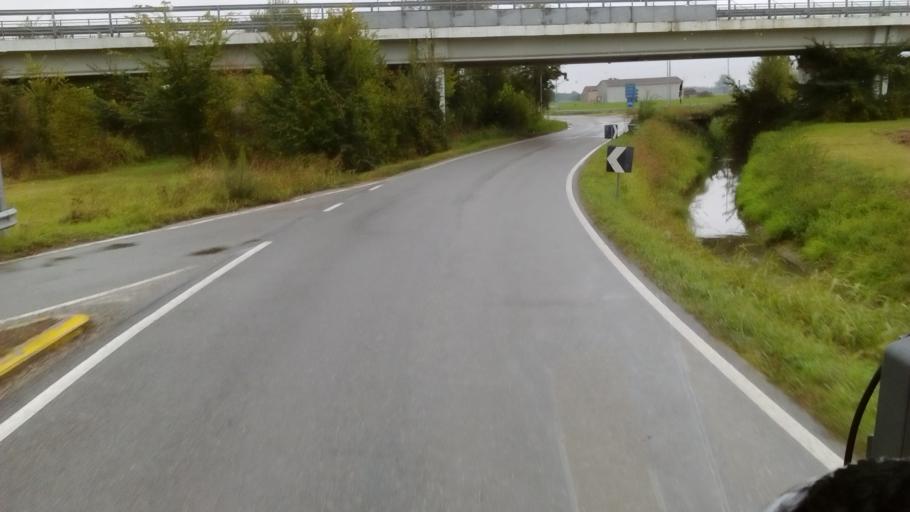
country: IT
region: Emilia-Romagna
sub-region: Provincia di Reggio Emilia
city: Luzzara
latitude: 44.9466
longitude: 10.7117
